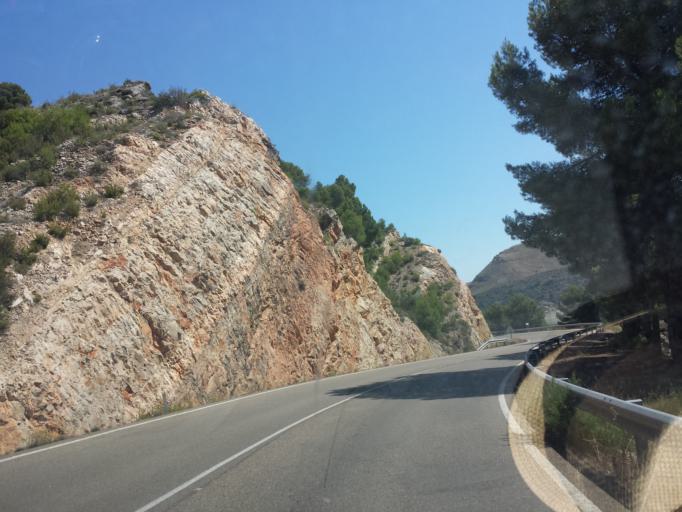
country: ES
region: Aragon
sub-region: Provincia de Zaragoza
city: Ibdes
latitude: 41.2424
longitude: -1.8150
